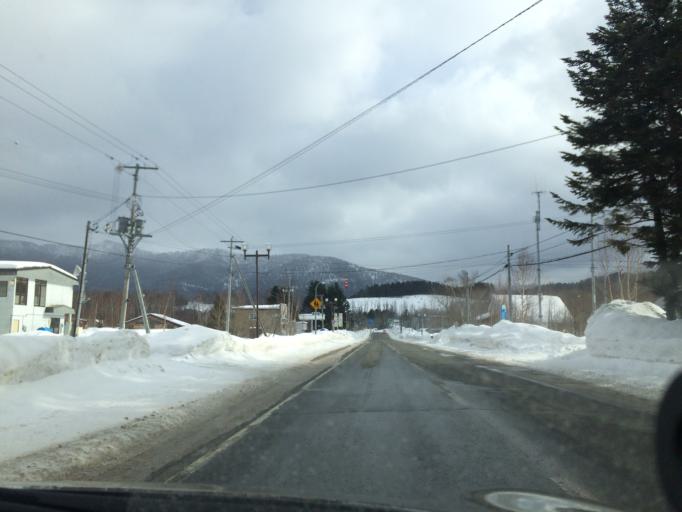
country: JP
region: Hokkaido
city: Shimo-furano
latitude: 43.0450
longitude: 142.6526
